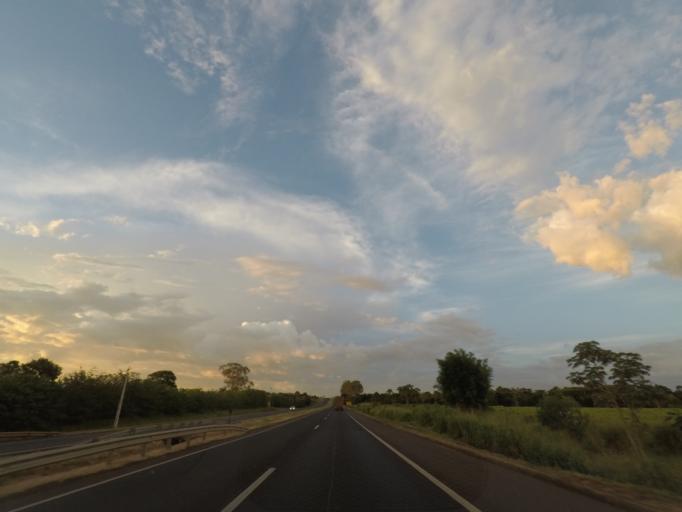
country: BR
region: Minas Gerais
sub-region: Uberaba
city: Uberaba
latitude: -19.6782
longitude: -47.9953
